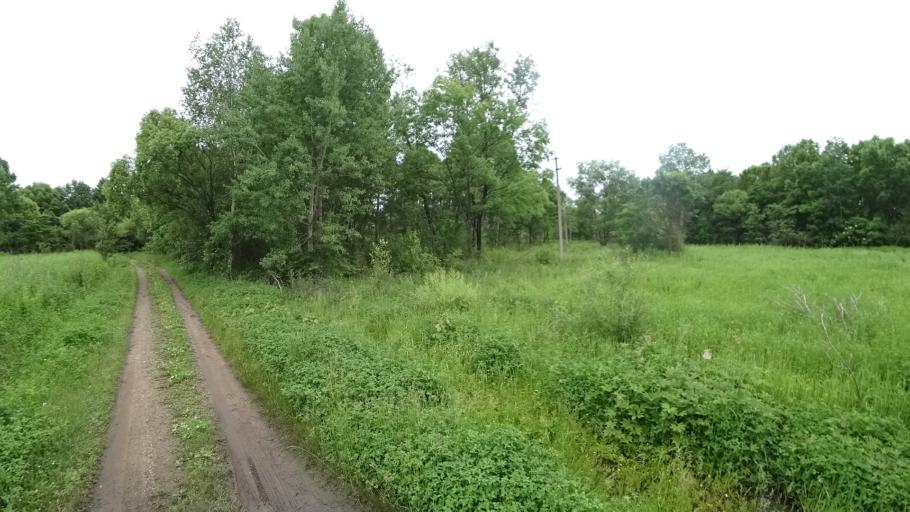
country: RU
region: Primorskiy
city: Novosysoyevka
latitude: 44.2032
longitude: 133.3211
